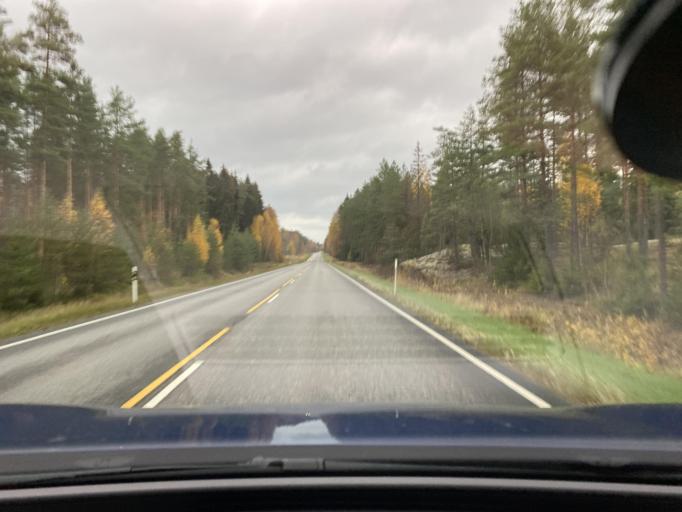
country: FI
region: Varsinais-Suomi
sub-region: Loimaa
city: Ylaene
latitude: 60.8943
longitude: 22.4051
